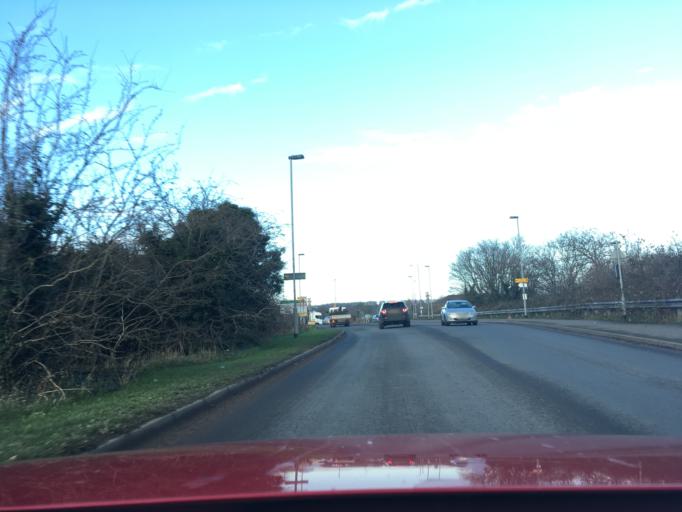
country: GB
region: England
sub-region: Staffordshire
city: Burton upon Trent
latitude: 52.7881
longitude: -1.6711
